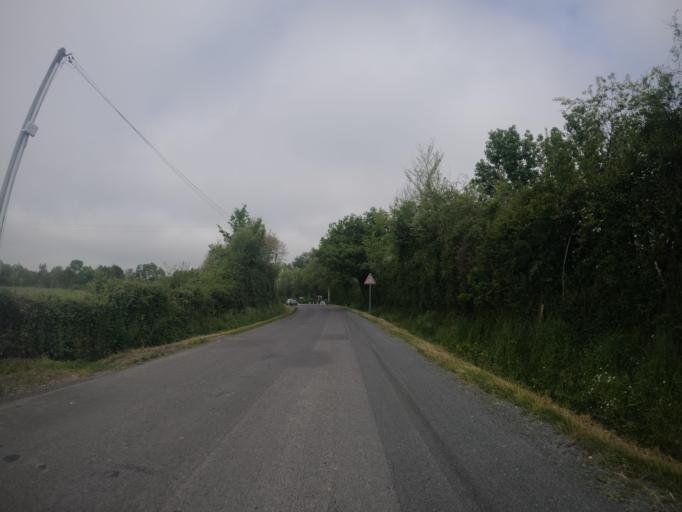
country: FR
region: Poitou-Charentes
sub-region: Departement des Deux-Sevres
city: Chiche
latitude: 46.8286
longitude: -0.3573
